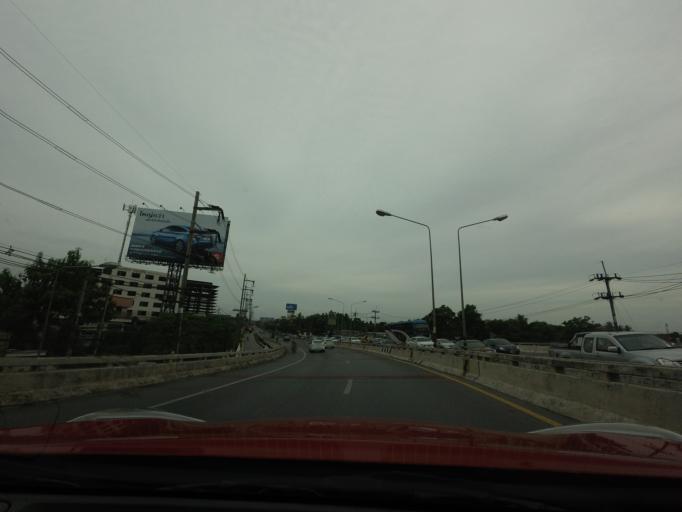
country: TH
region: Songkhla
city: Hat Yai
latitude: 6.9872
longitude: 100.4804
